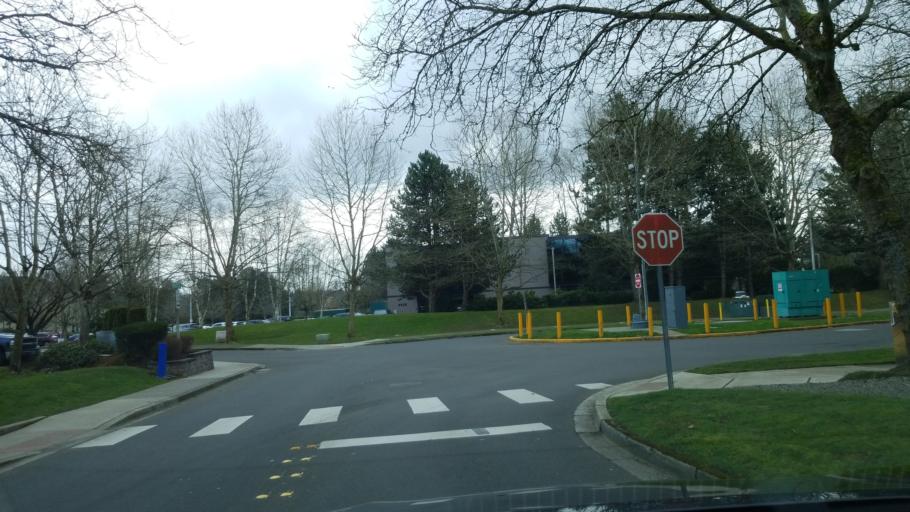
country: US
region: Washington
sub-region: King County
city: Tukwila
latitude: 47.4675
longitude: -122.2481
